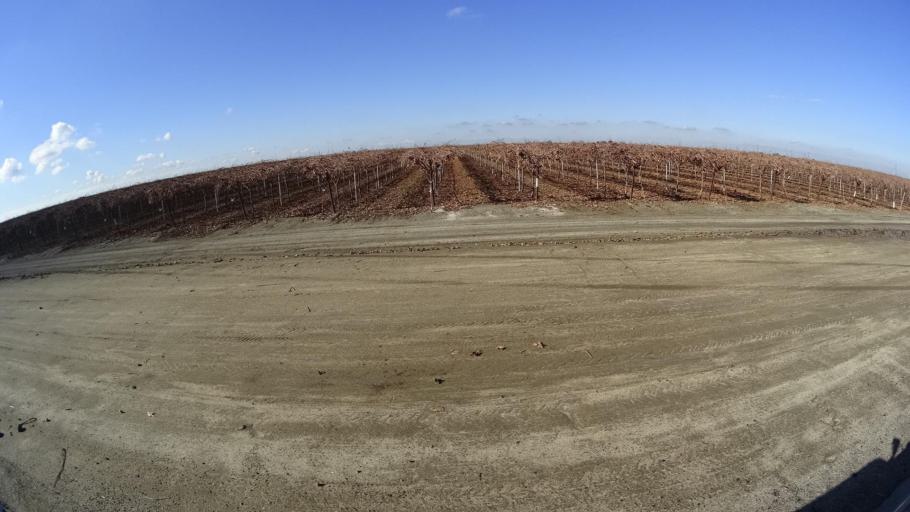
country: US
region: California
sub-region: Kern County
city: McFarland
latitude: 35.7147
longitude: -119.2586
